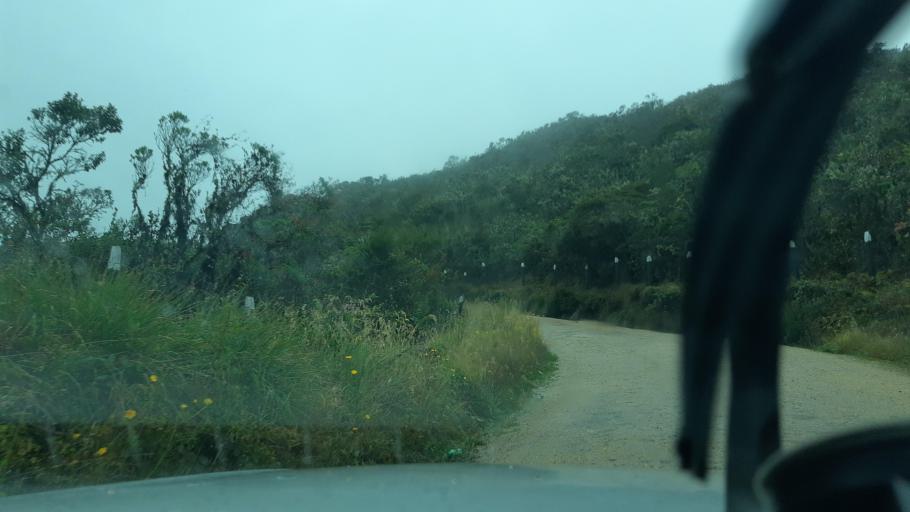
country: CO
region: Cundinamarca
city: Umbita
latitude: 5.2151
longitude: -73.5237
